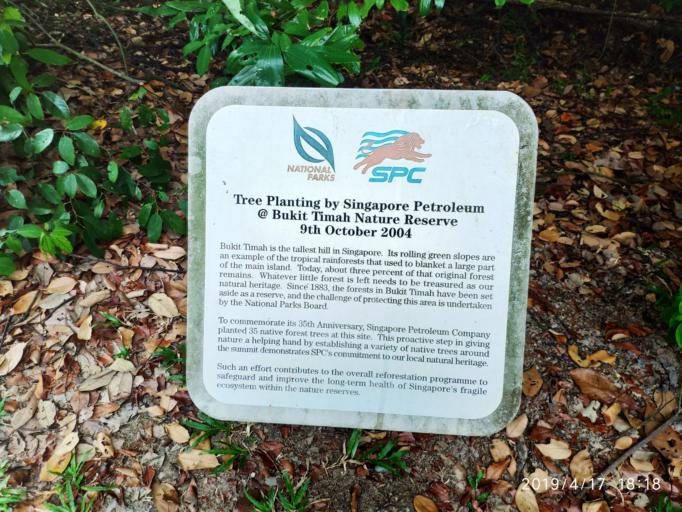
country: SG
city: Singapore
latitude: 1.3546
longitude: 103.7764
